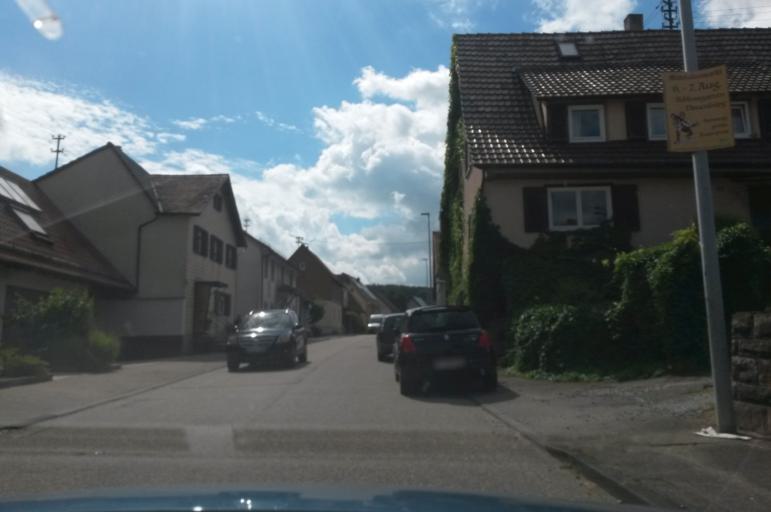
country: DE
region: Baden-Wuerttemberg
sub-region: Karlsruhe Region
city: Dobel
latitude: 48.8579
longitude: 8.5300
